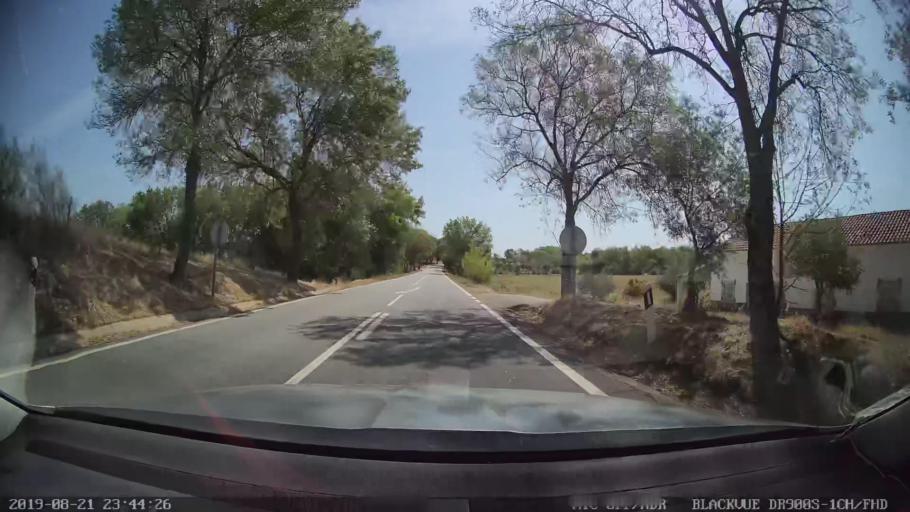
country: PT
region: Castelo Branco
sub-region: Idanha-A-Nova
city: Idanha-a-Nova
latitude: 39.8460
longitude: -7.2786
